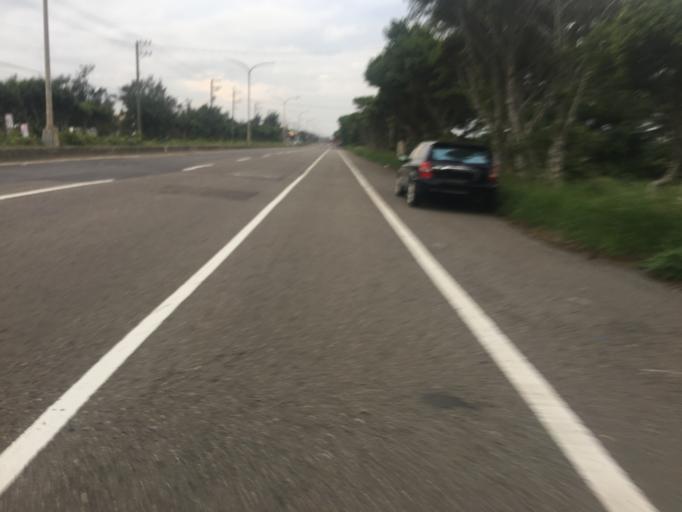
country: TW
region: Taiwan
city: Taoyuan City
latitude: 25.0847
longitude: 121.2213
